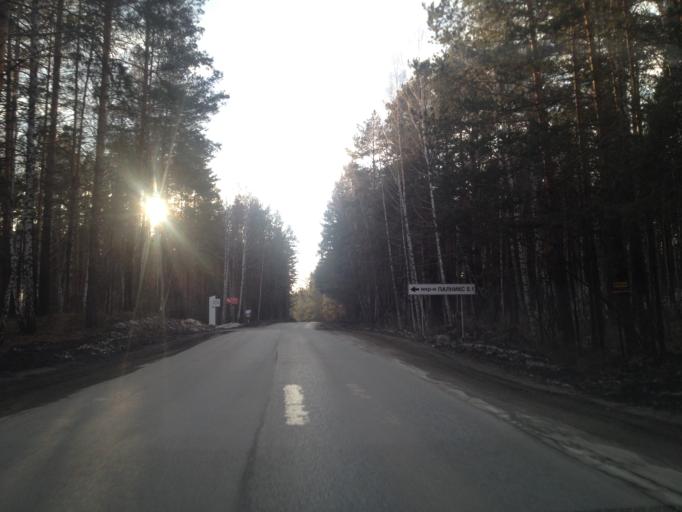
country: RU
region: Sverdlovsk
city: Shirokaya Rechka
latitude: 56.8147
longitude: 60.4367
